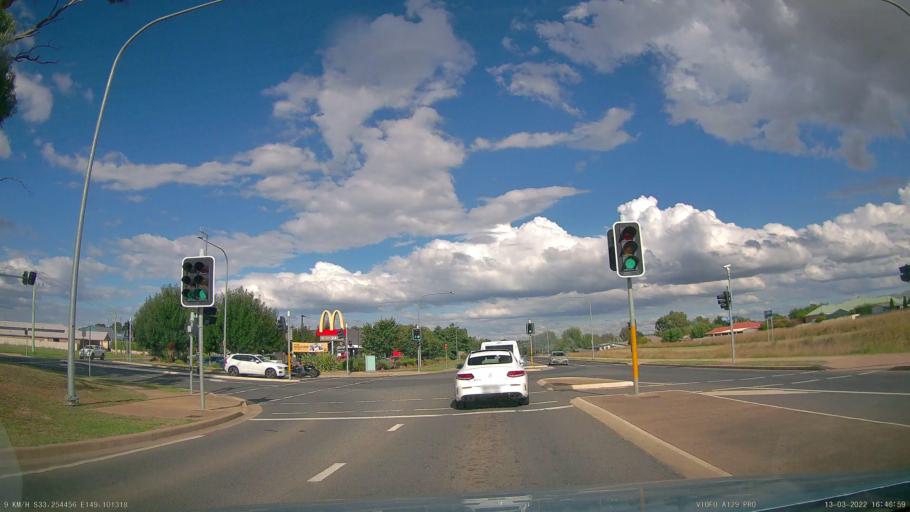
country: AU
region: New South Wales
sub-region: Orange Municipality
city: Orange
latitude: -33.2545
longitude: 149.1013
